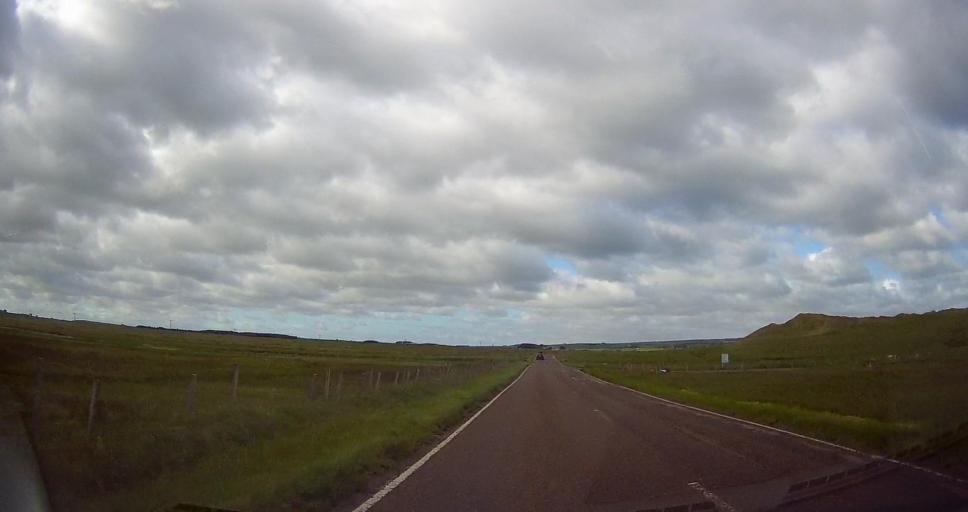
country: GB
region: Scotland
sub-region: Highland
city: Thurso
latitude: 58.6017
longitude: -3.3498
